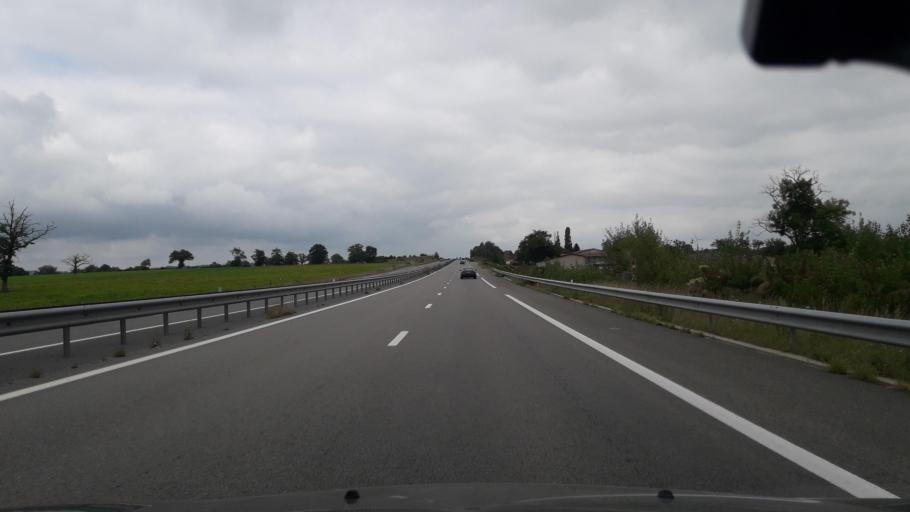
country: FR
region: Limousin
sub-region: Departement de la Creuse
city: Chambon-sur-Voueize
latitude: 46.2752
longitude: 2.3861
